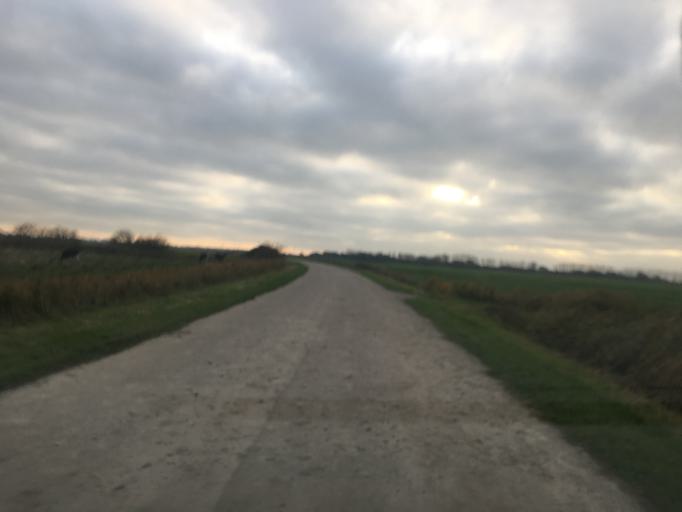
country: DE
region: Schleswig-Holstein
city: Neukirchen
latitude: 54.9172
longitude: 8.7553
